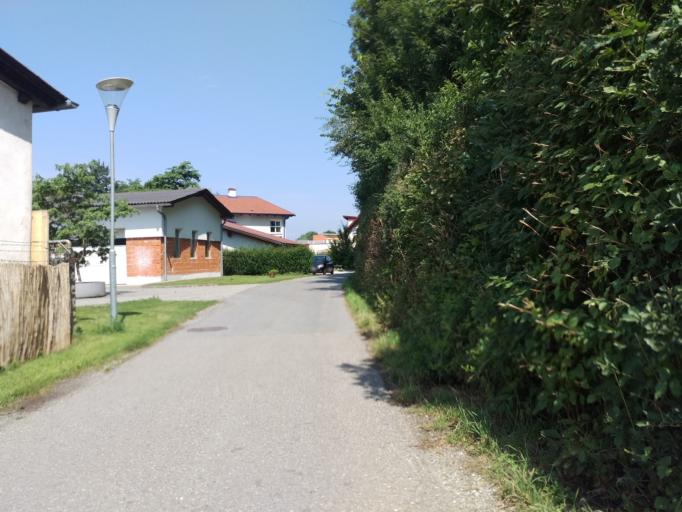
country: AT
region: Styria
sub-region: Politischer Bezirk Graz-Umgebung
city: Gossendorf
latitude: 46.9851
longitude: 15.4703
